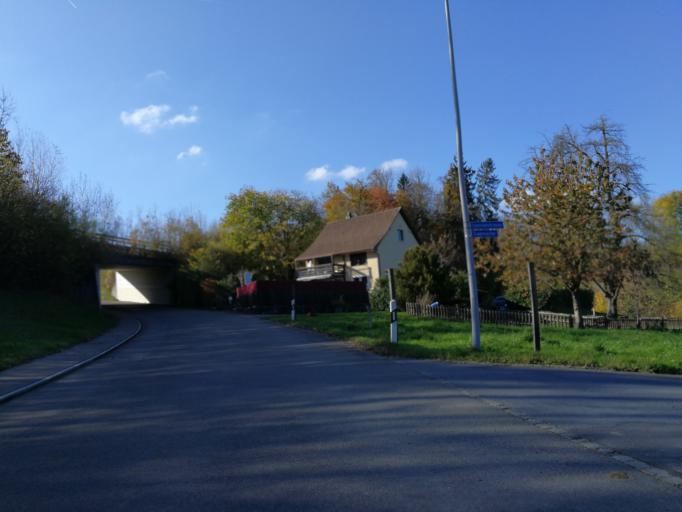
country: CH
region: Zurich
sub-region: Bezirk Uster
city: Egg
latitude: 47.2995
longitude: 8.7007
